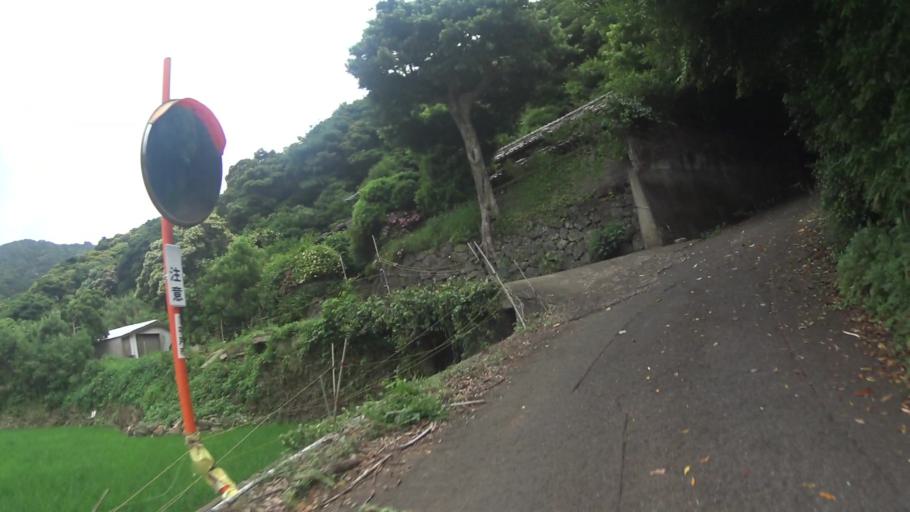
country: JP
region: Nagasaki
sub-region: Hirado Shi
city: Hirado
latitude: 33.1852
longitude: 129.3641
